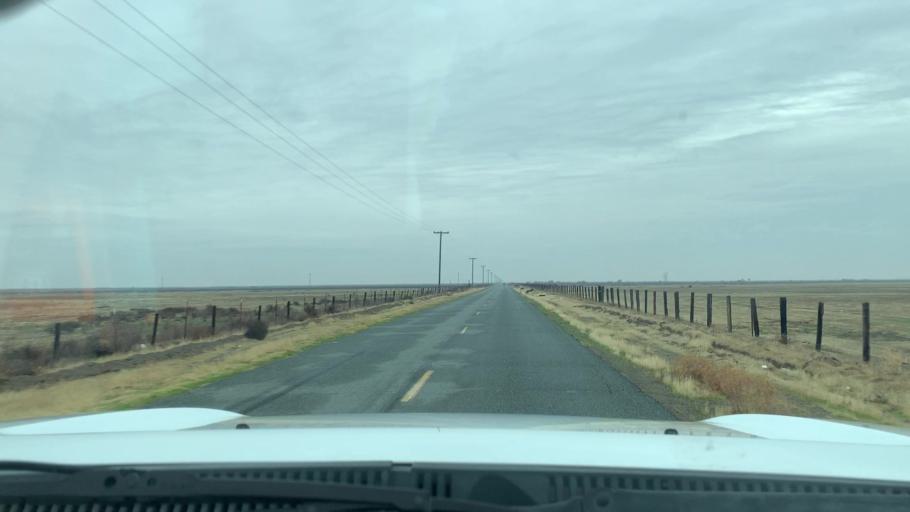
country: US
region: California
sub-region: Tulare County
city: Alpaugh
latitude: 35.7610
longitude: -119.5517
